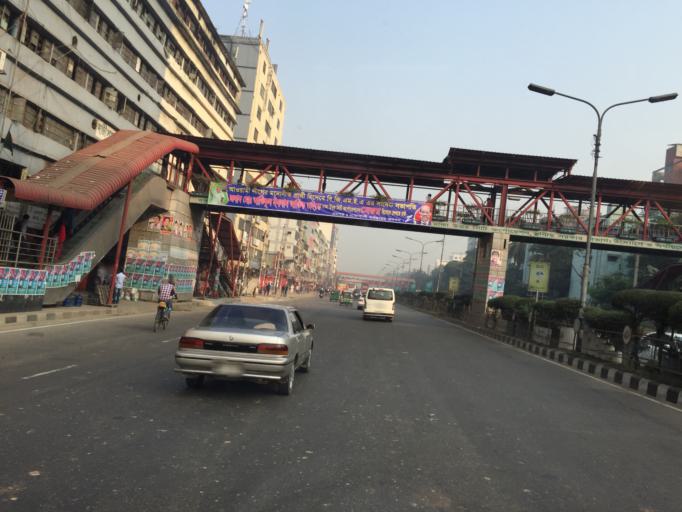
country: BD
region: Dhaka
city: Paltan
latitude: 23.7915
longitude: 90.4004
